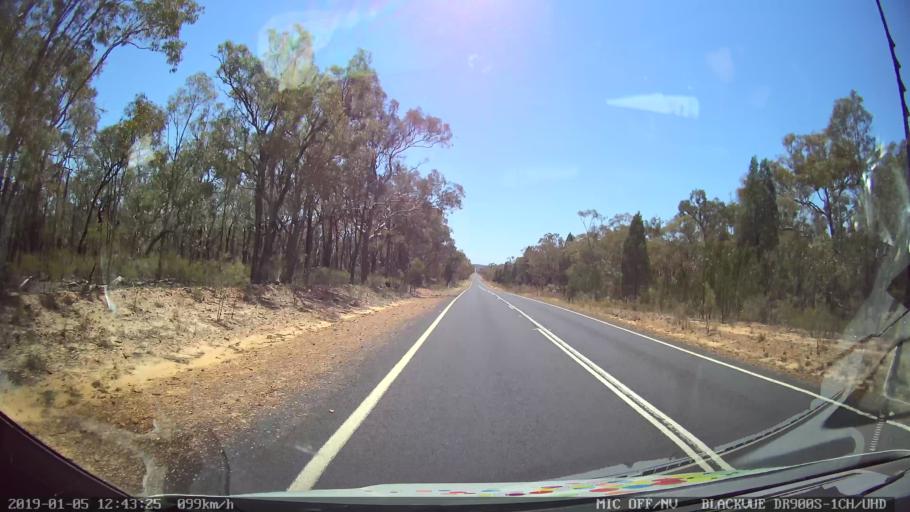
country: AU
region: New South Wales
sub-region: Warrumbungle Shire
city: Coonabarabran
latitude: -31.1482
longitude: 149.5239
